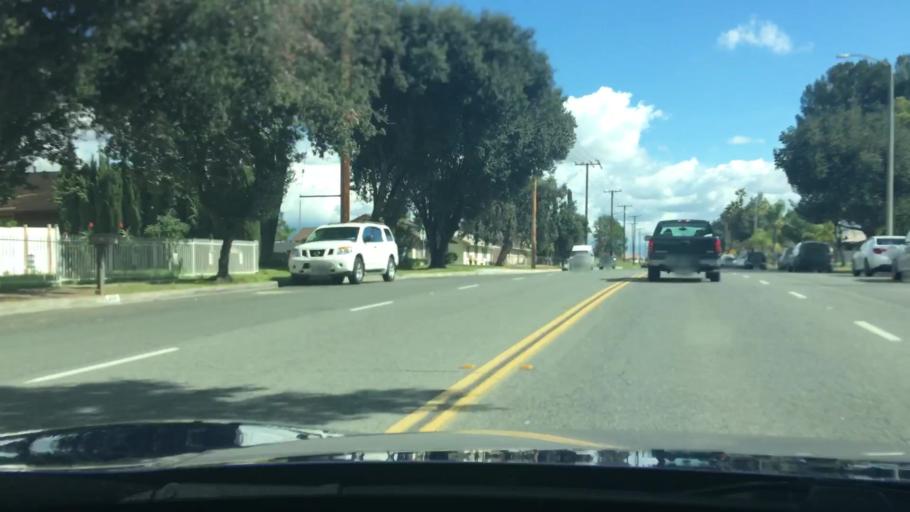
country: US
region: California
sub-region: San Bernardino County
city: Rialto
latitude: 34.0851
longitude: -117.3646
